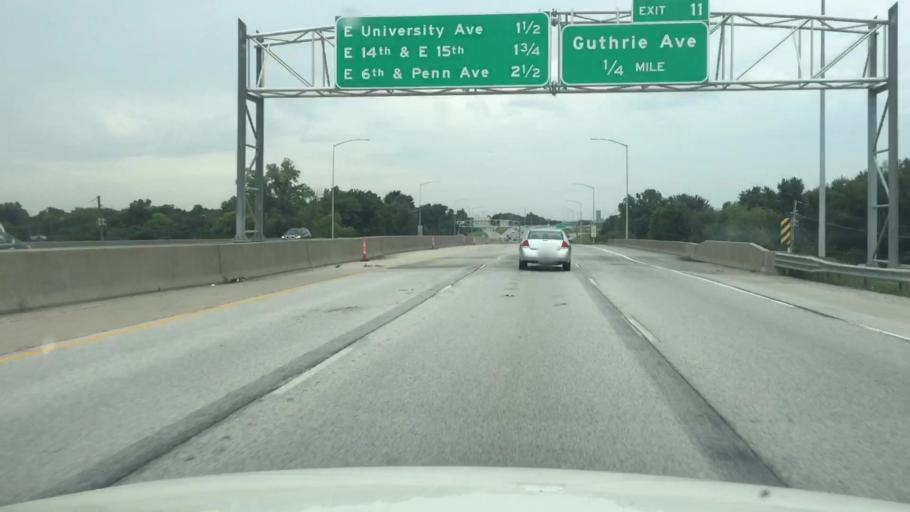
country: US
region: Iowa
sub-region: Polk County
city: Des Moines
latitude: 41.6230
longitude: -93.5761
